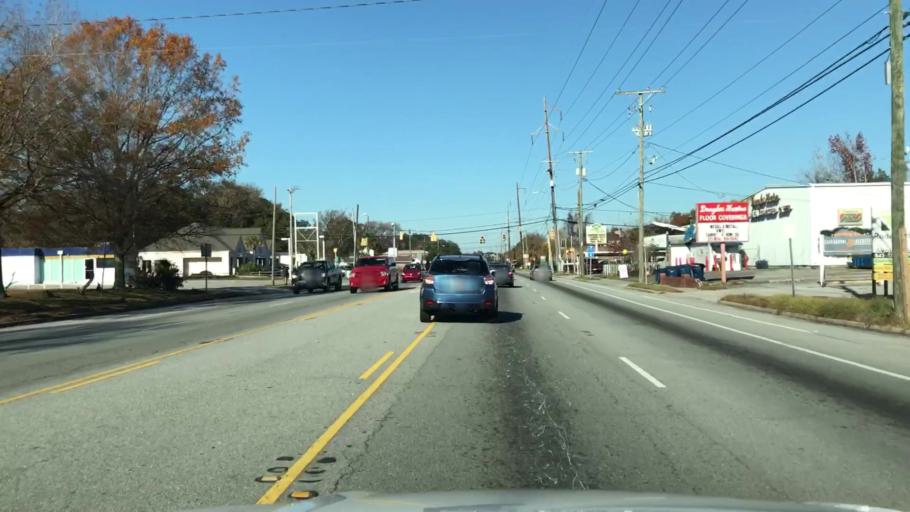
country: US
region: South Carolina
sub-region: Charleston County
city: Charleston
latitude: 32.7915
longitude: -79.9879
